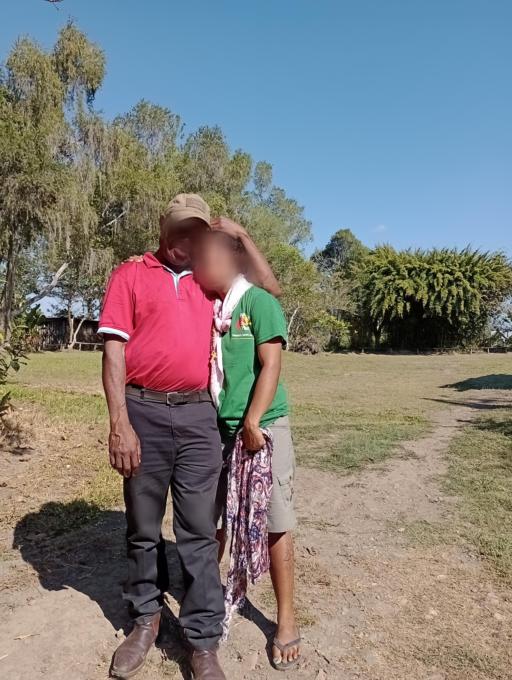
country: PG
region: Jiwaka
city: Minj
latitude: -5.8065
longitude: 144.6751
